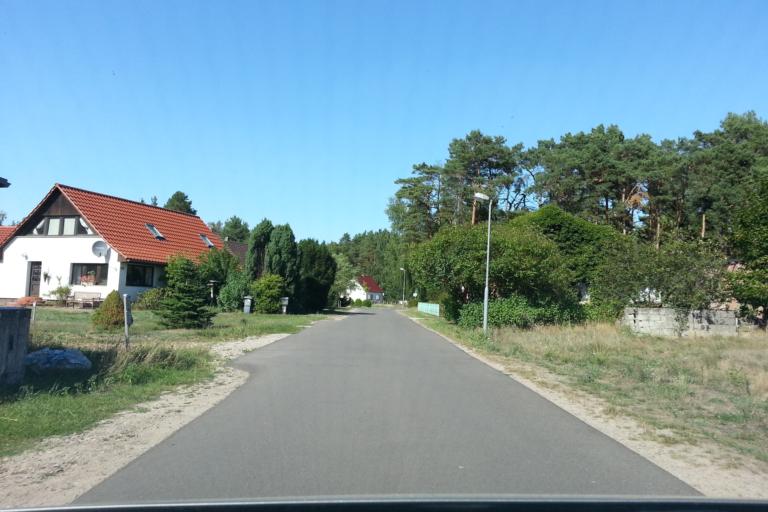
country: DE
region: Mecklenburg-Vorpommern
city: Eggesin
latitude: 53.6858
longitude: 14.0438
